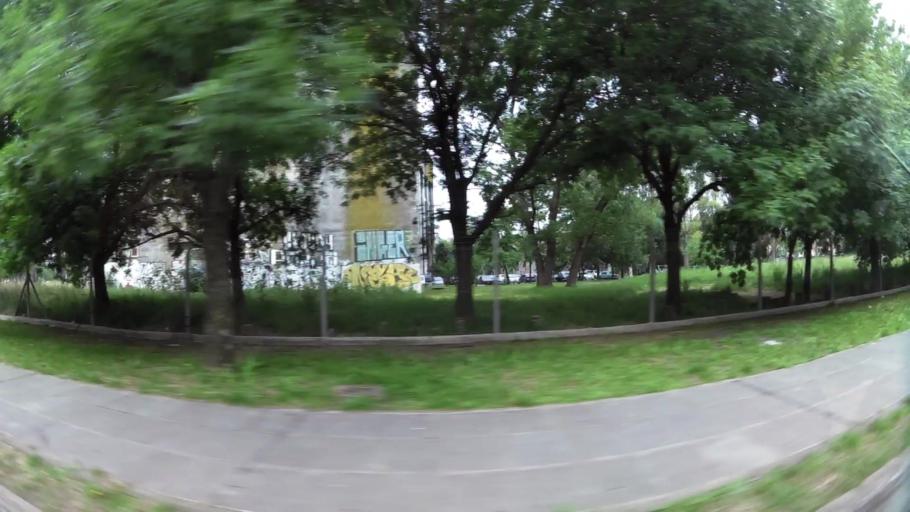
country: AR
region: Buenos Aires
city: San Justo
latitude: -34.6974
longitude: -58.5782
